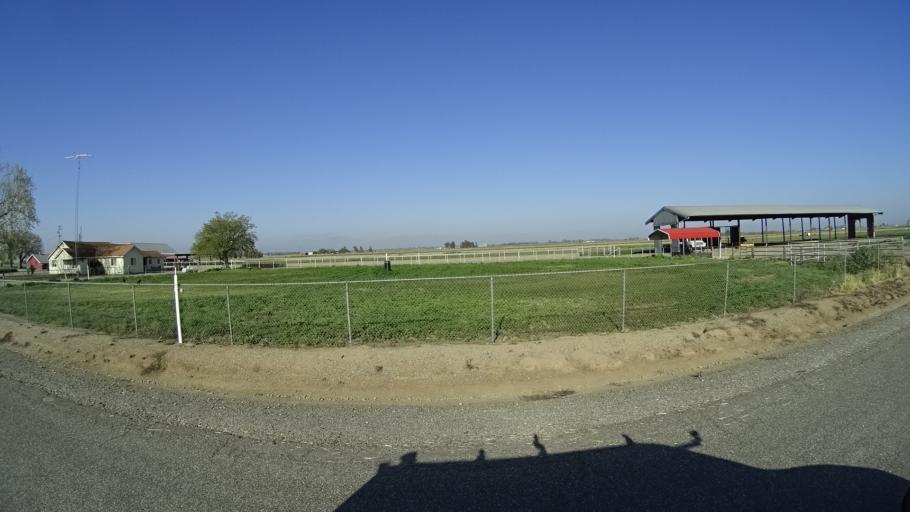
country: US
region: California
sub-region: Glenn County
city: Willows
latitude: 39.5329
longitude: -122.1215
